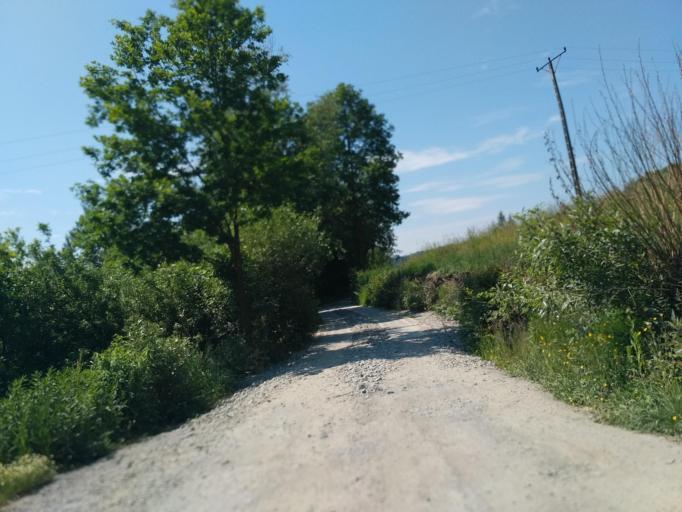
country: PL
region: Subcarpathian Voivodeship
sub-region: Powiat strzyzowski
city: Gwoznica Gorna
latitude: 49.8170
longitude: 22.0465
